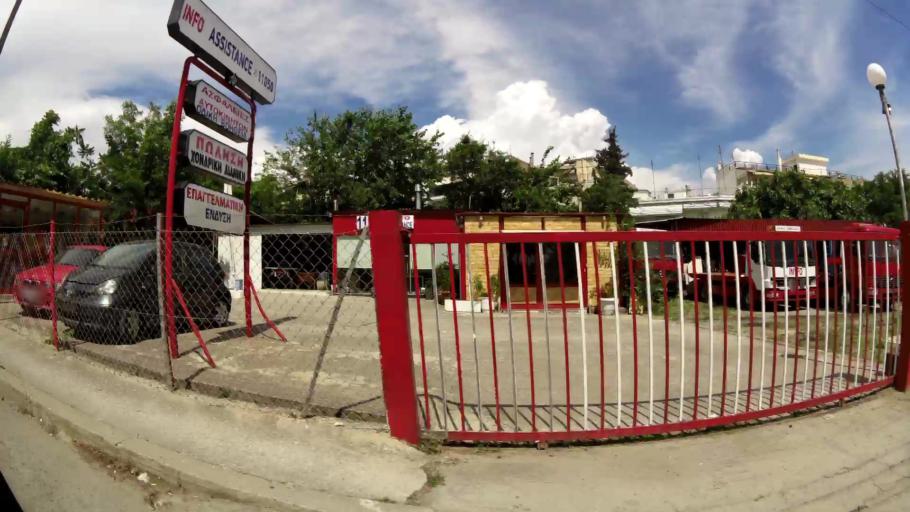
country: GR
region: Central Macedonia
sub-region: Nomos Thessalonikis
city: Pylaia
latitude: 40.5948
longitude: 22.9717
